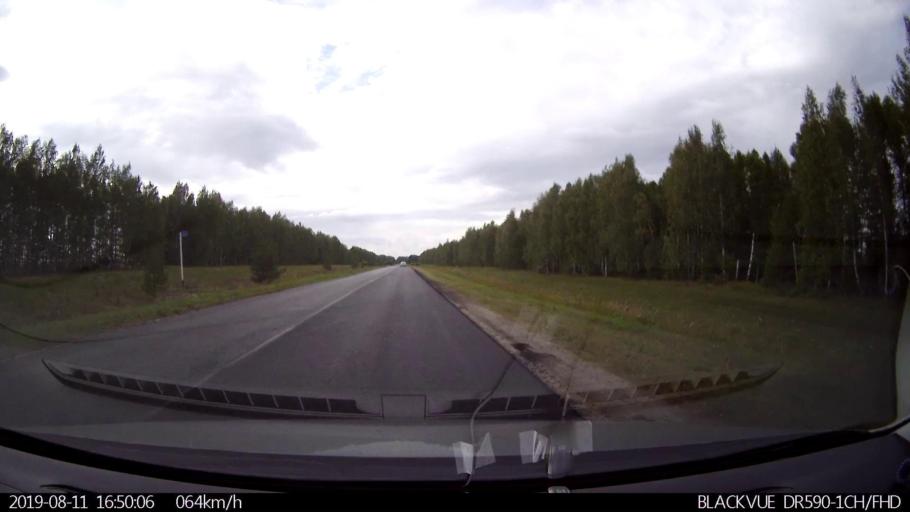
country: RU
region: Ulyanovsk
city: Mayna
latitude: 54.2259
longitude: 47.6912
